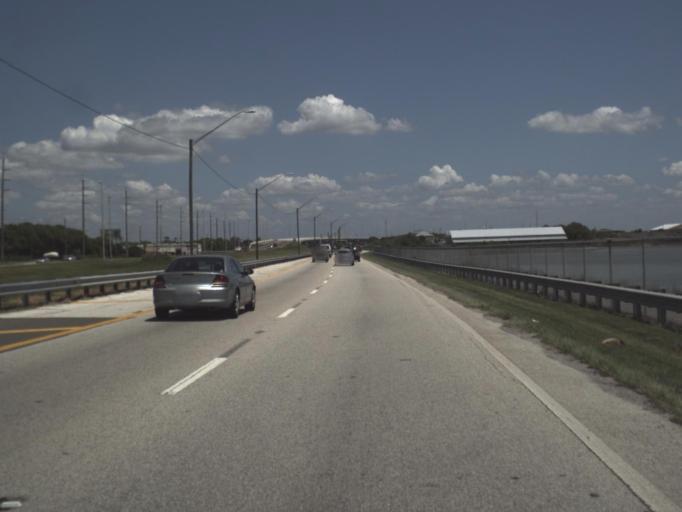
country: US
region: Florida
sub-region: Pinellas County
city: Pinellas Park
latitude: 27.8788
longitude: -82.6875
